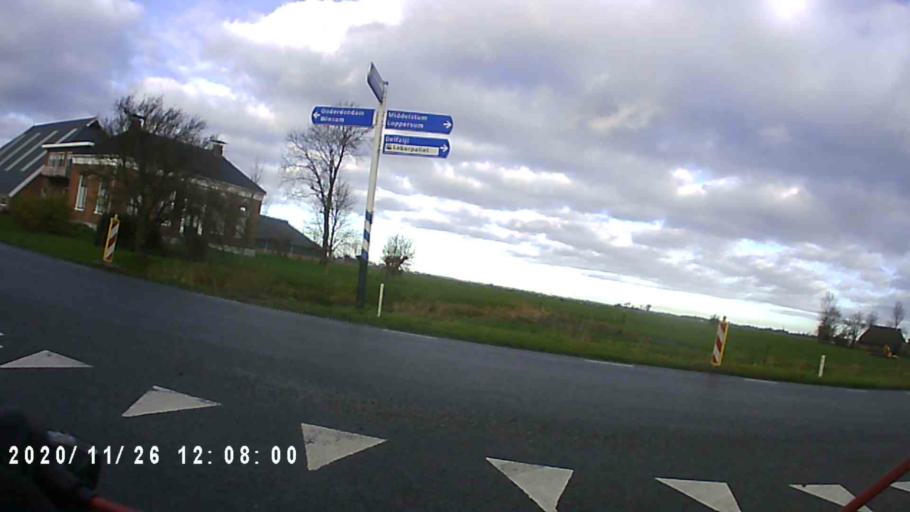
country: NL
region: Groningen
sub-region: Gemeente Bedum
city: Bedum
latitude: 53.3390
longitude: 6.6279
